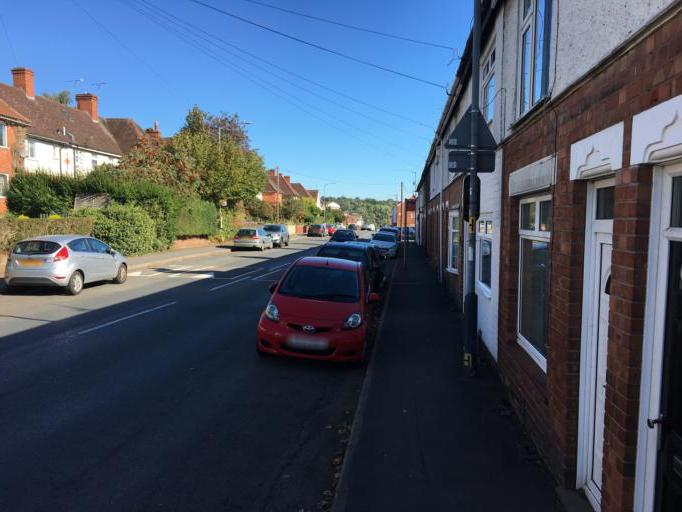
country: GB
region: England
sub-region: Warwickshire
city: Kenilworth
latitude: 52.3476
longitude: -1.5747
